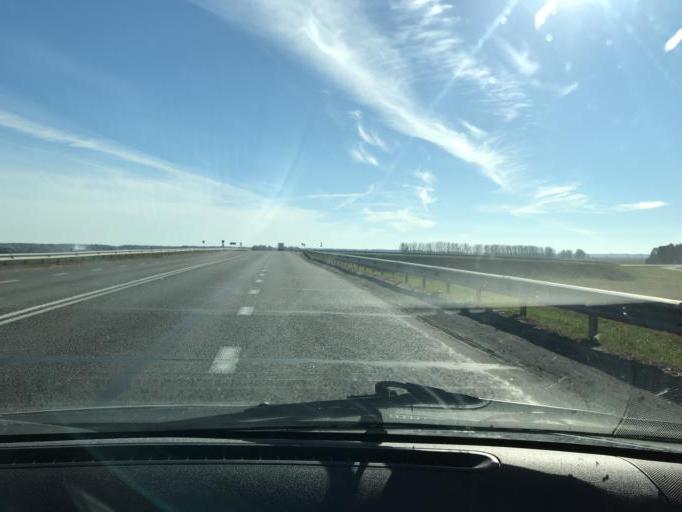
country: BY
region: Brest
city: Ivatsevichy
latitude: 52.7019
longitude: 25.3613
